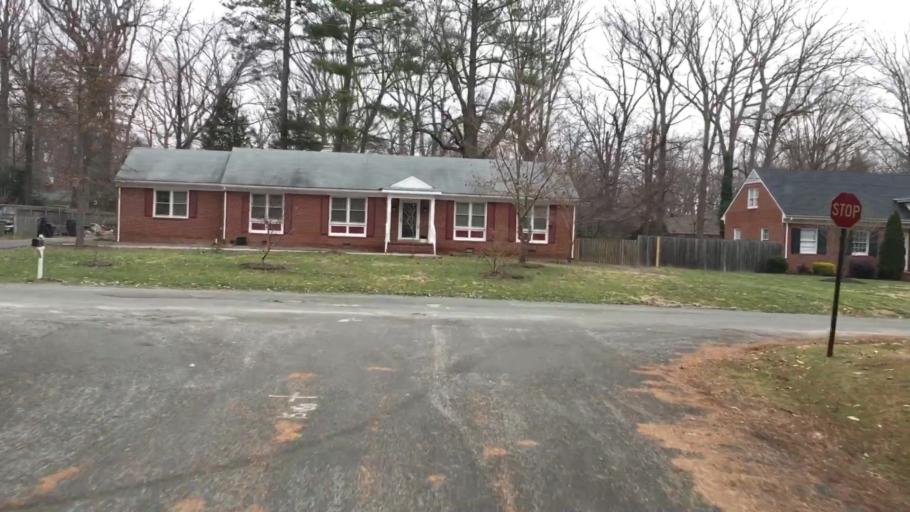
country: US
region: Virginia
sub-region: Chesterfield County
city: Bon Air
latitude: 37.5348
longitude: -77.5779
